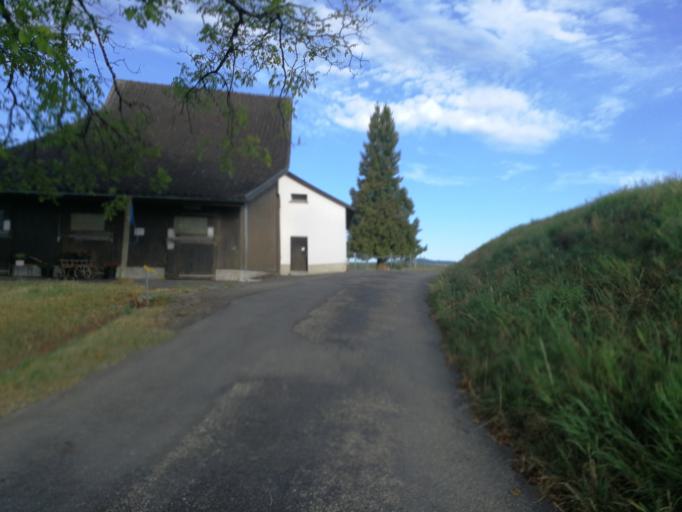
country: CH
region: Zurich
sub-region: Bezirk Meilen
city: Oetwil am See
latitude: 47.2629
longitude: 8.7402
